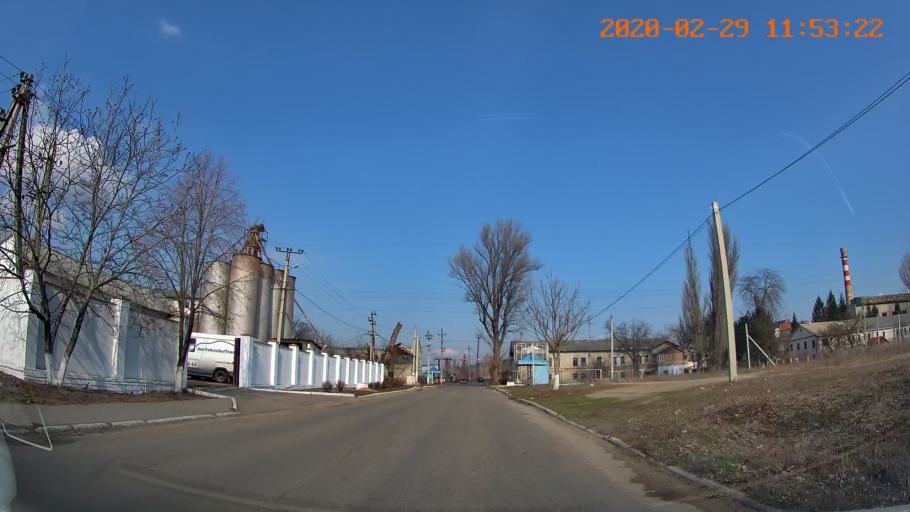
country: MD
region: Telenesti
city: Ribnita
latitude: 47.7768
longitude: 28.9908
